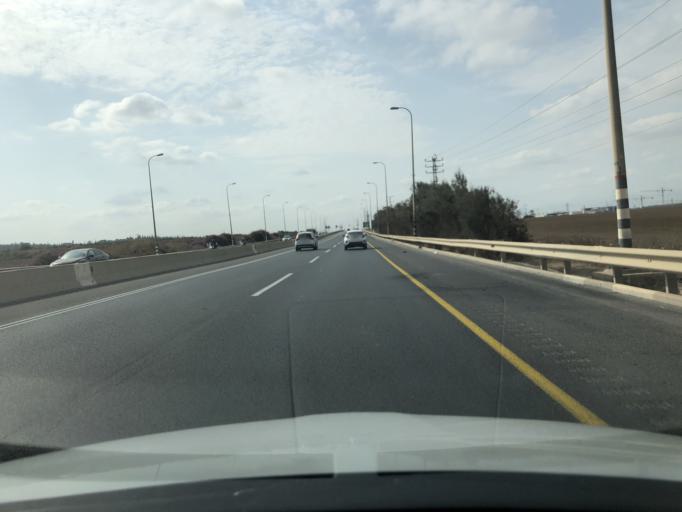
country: IL
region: Central District
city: Tirah
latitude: 32.2364
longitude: 34.9870
